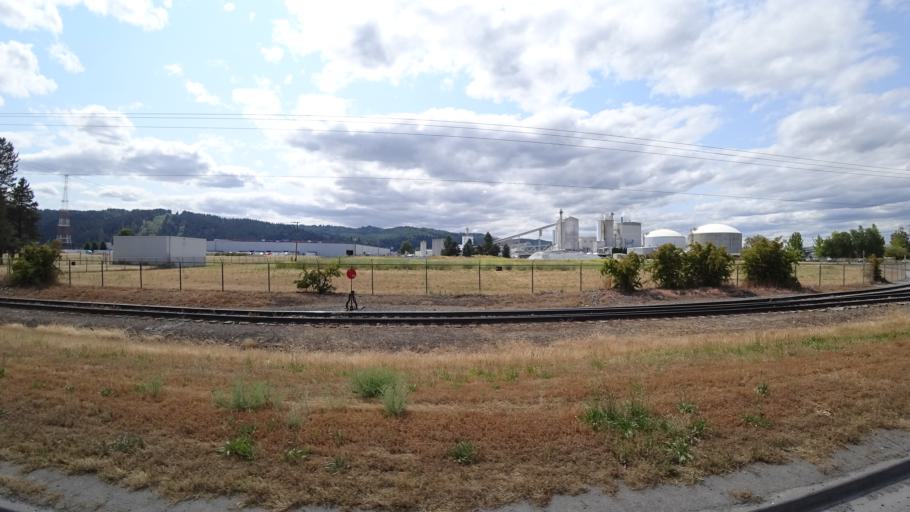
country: US
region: Oregon
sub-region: Washington County
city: Oak Hills
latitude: 45.6220
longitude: -122.7802
